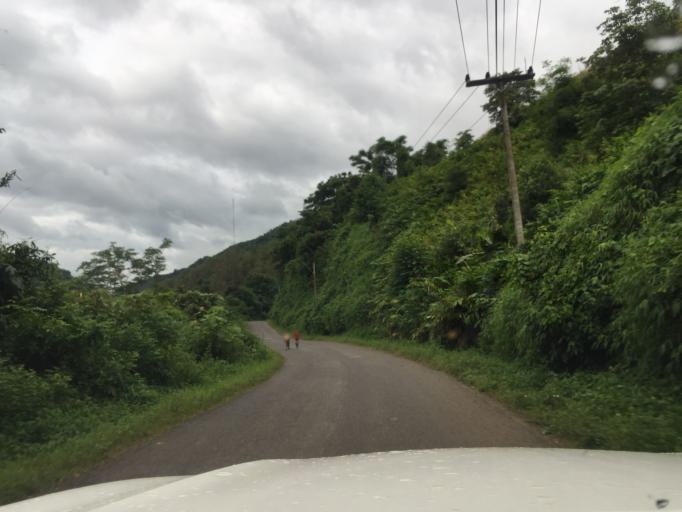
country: LA
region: Oudomxai
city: Muang La
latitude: 20.9924
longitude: 102.2294
